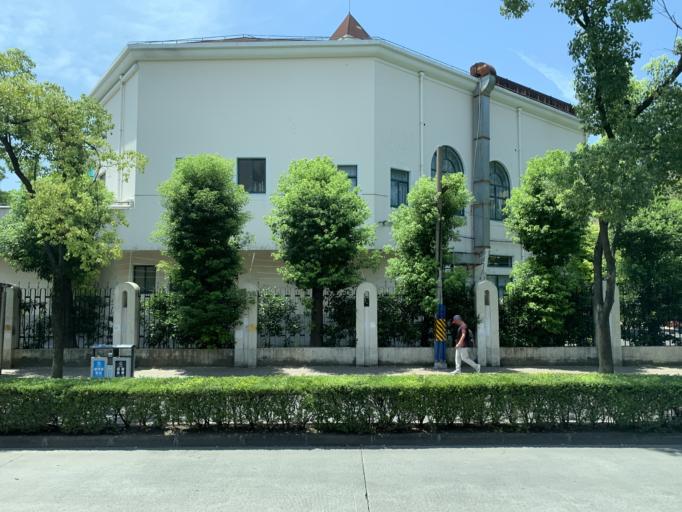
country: CN
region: Shanghai Shi
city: Huamu
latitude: 31.2509
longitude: 121.5787
